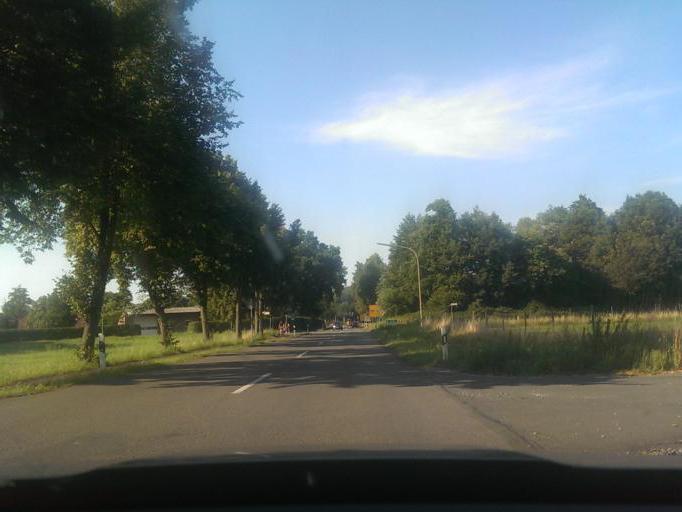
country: DE
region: North Rhine-Westphalia
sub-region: Regierungsbezirk Detmold
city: Delbruck
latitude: 51.7594
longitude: 8.5733
